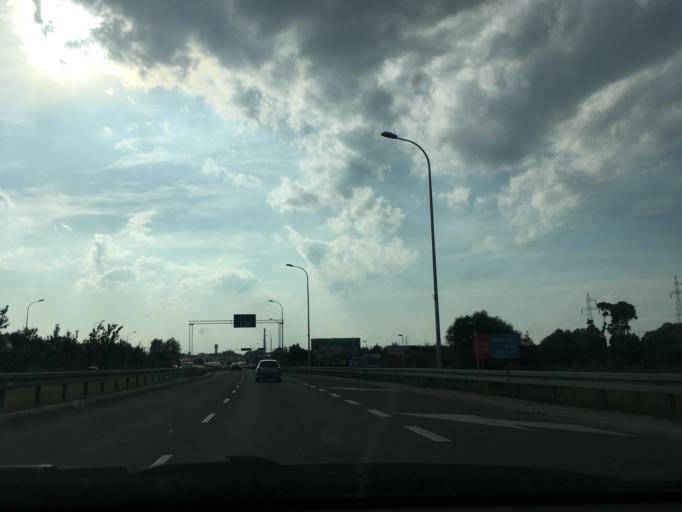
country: PL
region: Podlasie
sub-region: Bialystok
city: Bialystok
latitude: 53.1601
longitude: 23.1092
